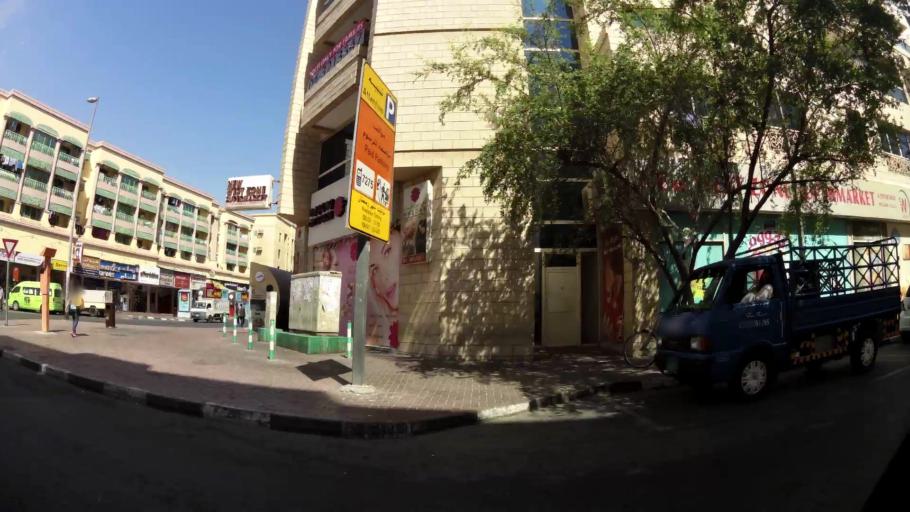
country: AE
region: Ash Shariqah
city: Sharjah
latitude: 25.2304
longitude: 55.2724
